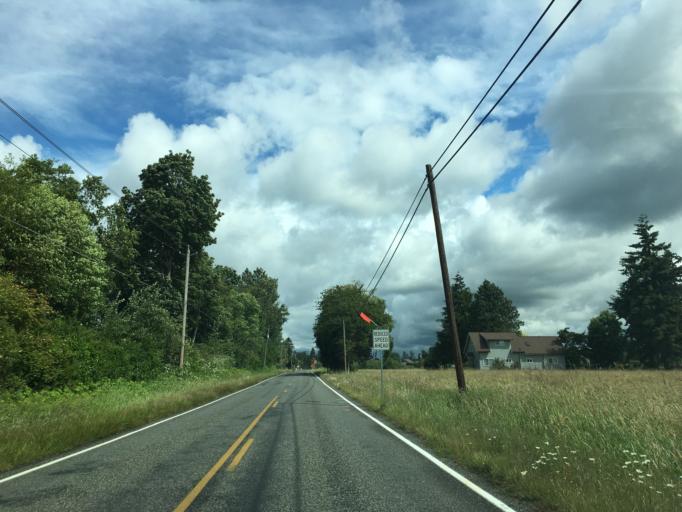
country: US
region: Washington
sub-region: Whatcom County
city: Birch Bay
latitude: 48.9041
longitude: -122.7487
